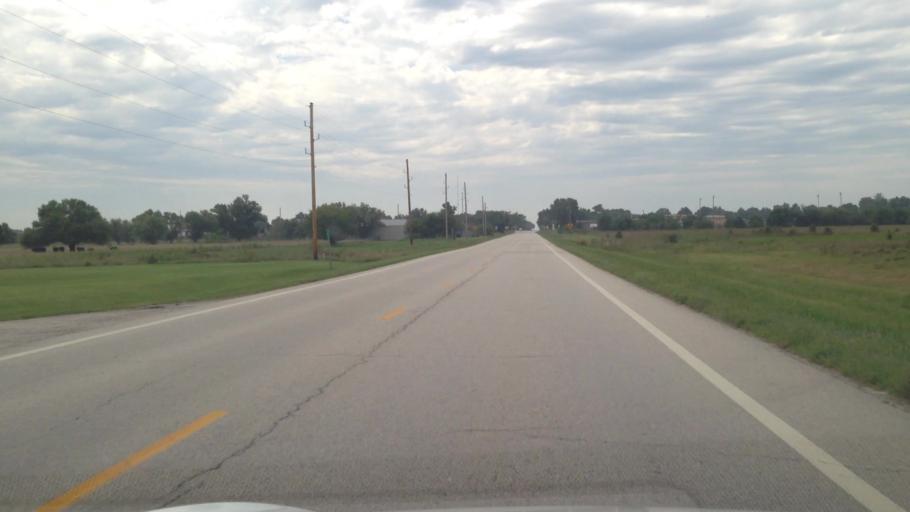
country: US
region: Kansas
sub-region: Allen County
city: Iola
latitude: 37.9268
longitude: -95.1701
